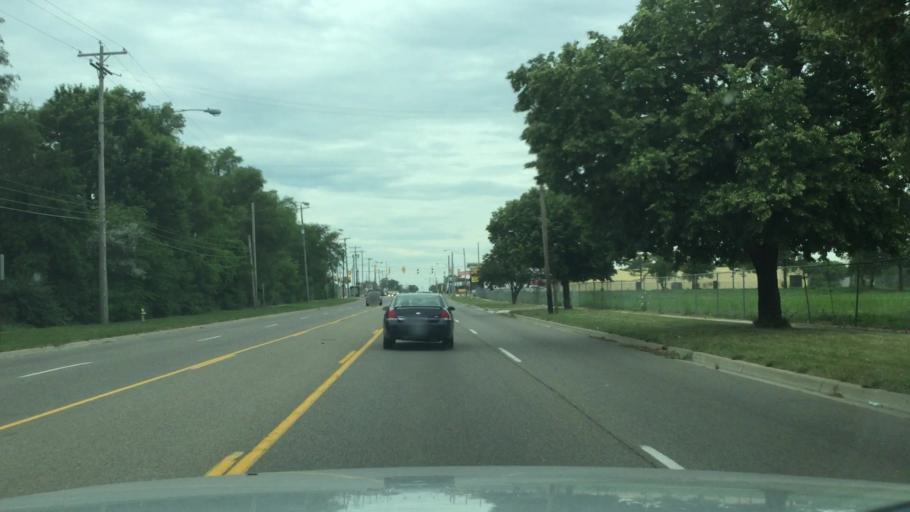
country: US
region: Michigan
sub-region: Genesee County
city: Beecher
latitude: 43.0607
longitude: -83.7271
